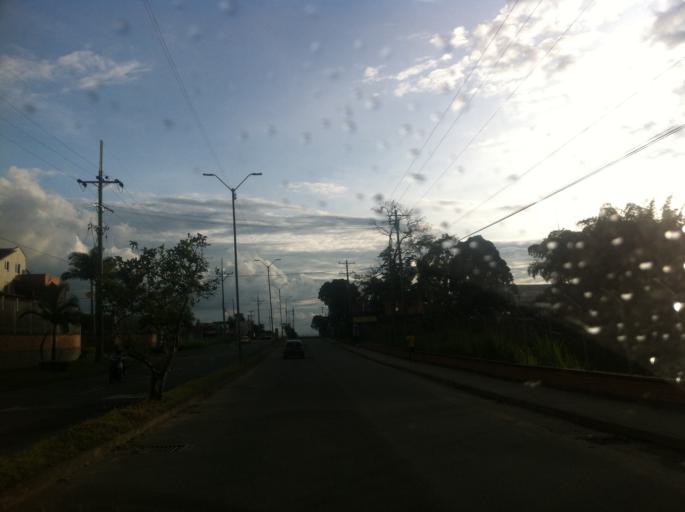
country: CO
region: Quindio
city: Calarca
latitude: 4.5723
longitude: -75.6399
